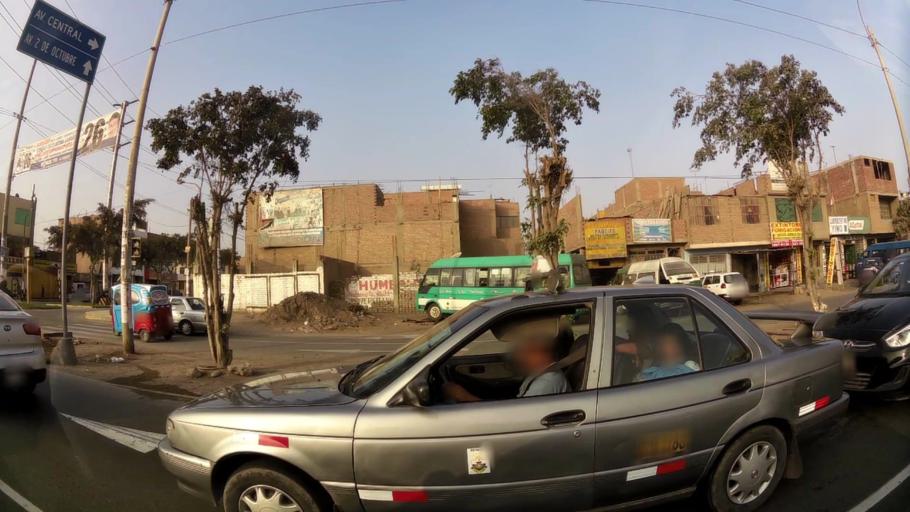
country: PE
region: Lima
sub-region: Lima
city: Independencia
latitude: -11.9552
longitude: -77.0847
